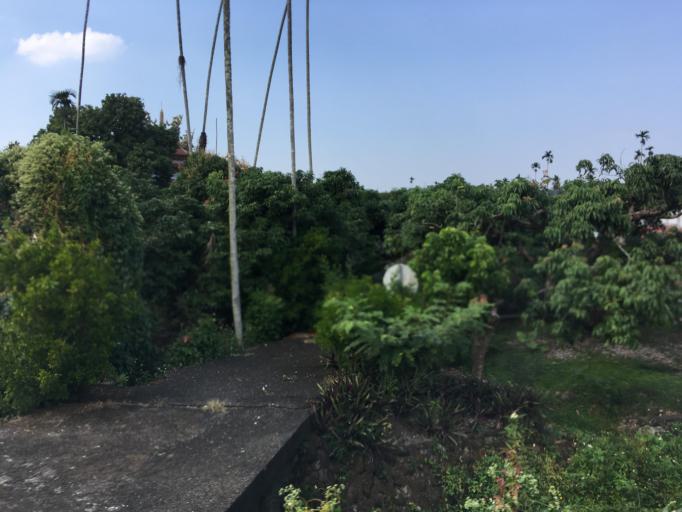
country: TW
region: Taiwan
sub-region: Chiayi
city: Jiayi Shi
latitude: 23.4922
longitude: 120.5205
